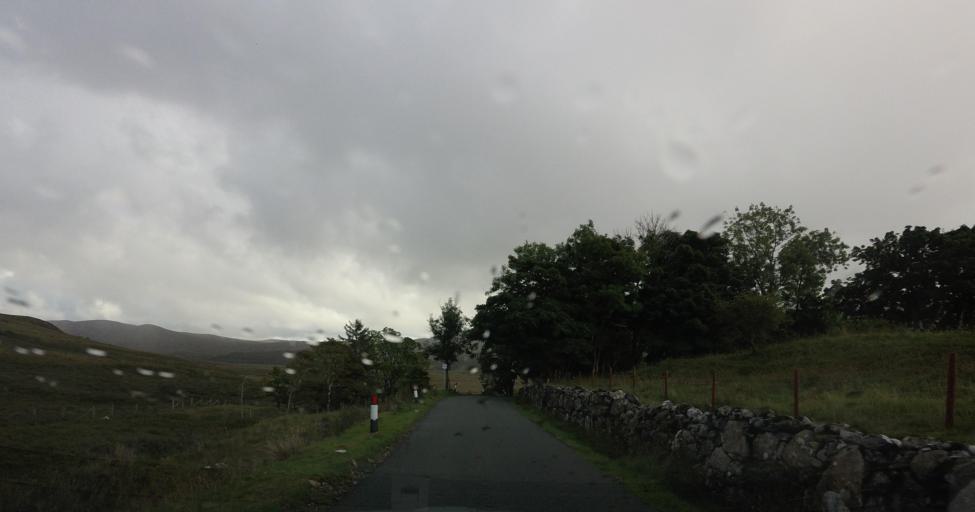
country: GB
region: Scotland
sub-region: Highland
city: Portree
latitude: 57.2108
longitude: -5.9890
